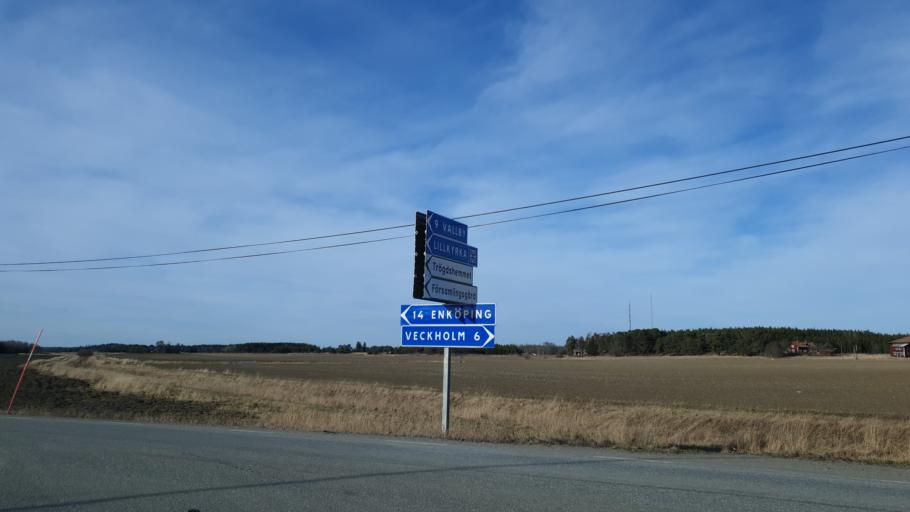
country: SE
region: Uppsala
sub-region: Enkopings Kommun
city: Grillby
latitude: 59.5611
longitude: 17.2470
